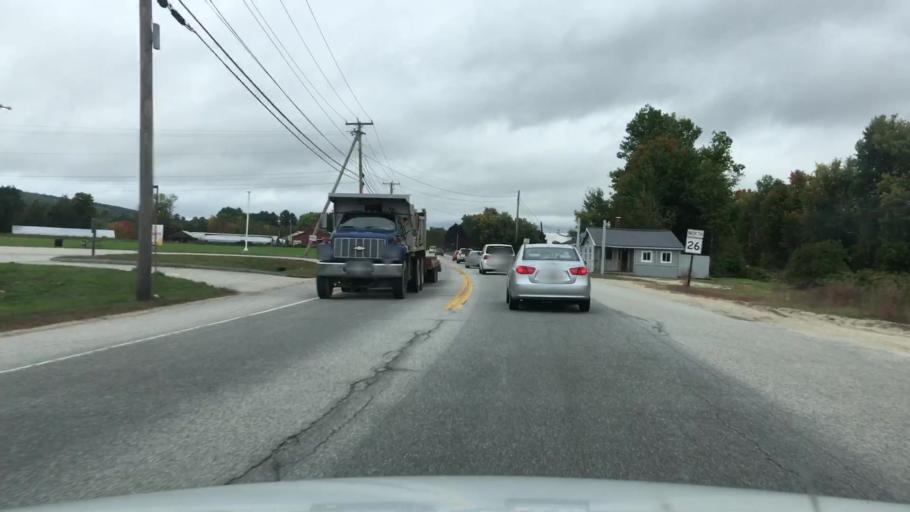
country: US
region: Maine
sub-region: Oxford County
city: South Paris
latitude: 44.1808
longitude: -70.5158
